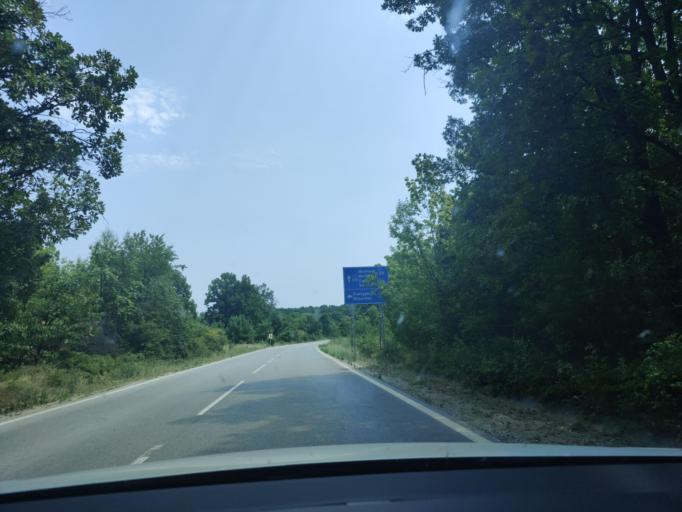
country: BG
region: Montana
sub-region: Obshtina Brusartsi
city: Brusartsi
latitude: 43.4940
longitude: 23.0513
